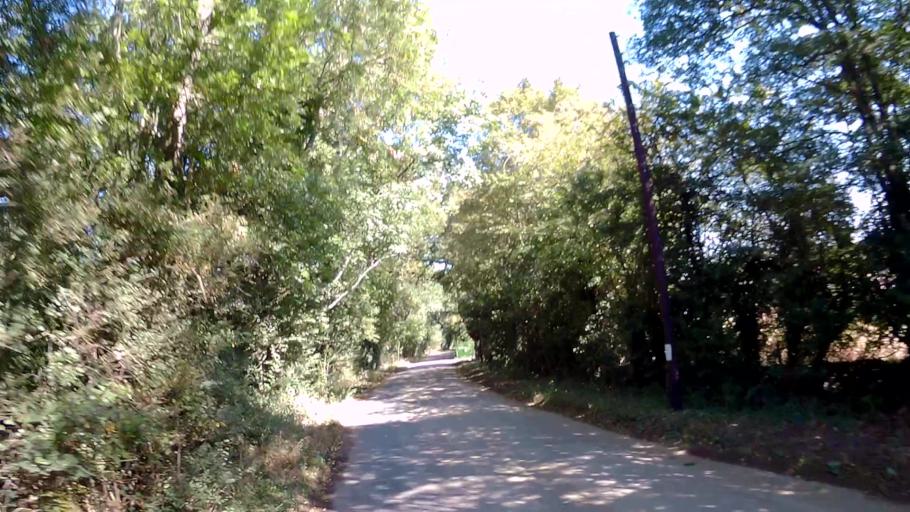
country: GB
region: England
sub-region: Hampshire
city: Eversley
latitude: 51.3760
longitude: -0.9021
